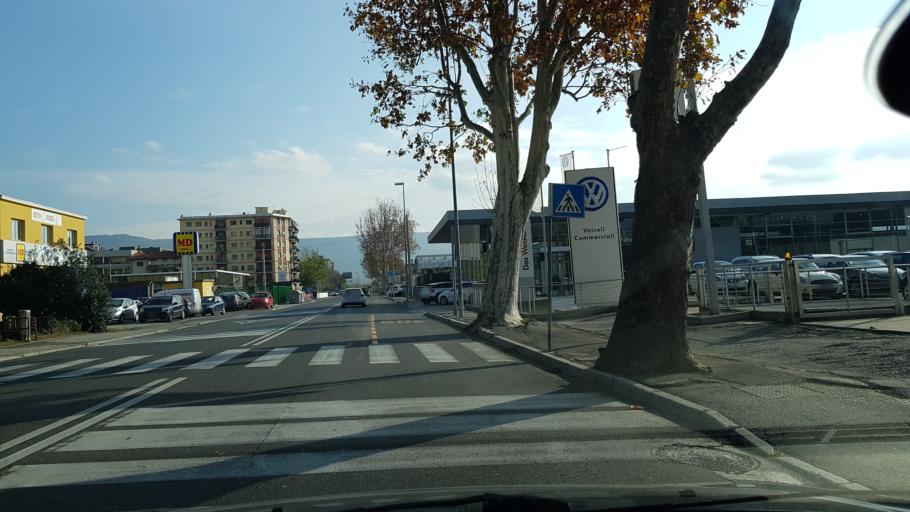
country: IT
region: Friuli Venezia Giulia
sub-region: Provincia di Trieste
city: Domio
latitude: 45.6213
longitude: 13.8077
